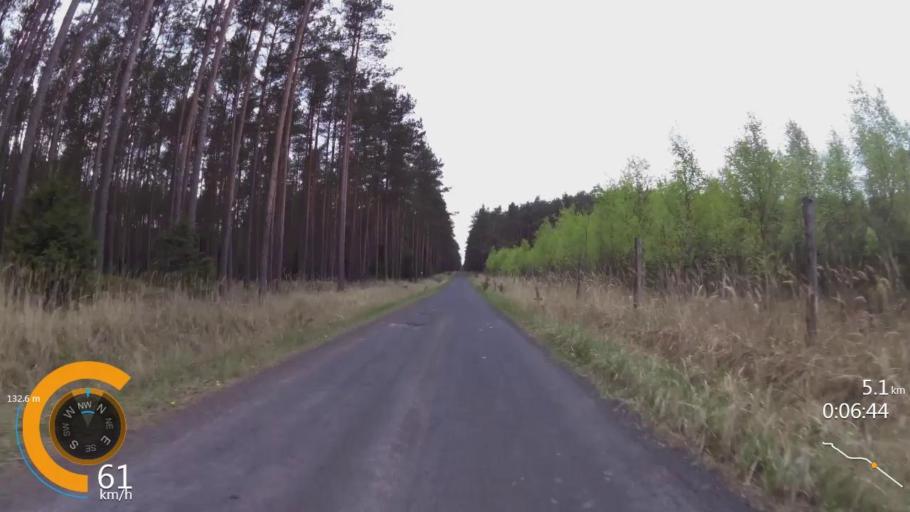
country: PL
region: West Pomeranian Voivodeship
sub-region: Powiat drawski
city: Wierzchowo
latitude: 53.4918
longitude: 16.1685
